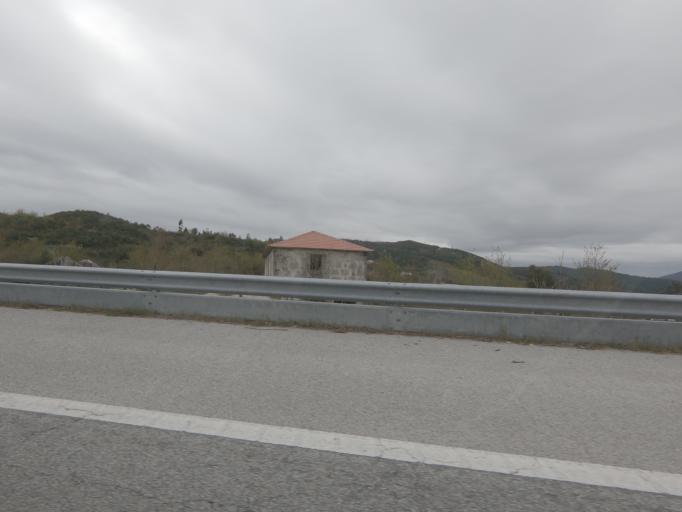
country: PT
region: Viseu
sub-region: Castro Daire
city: Castro Daire
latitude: 40.8922
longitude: -7.9281
